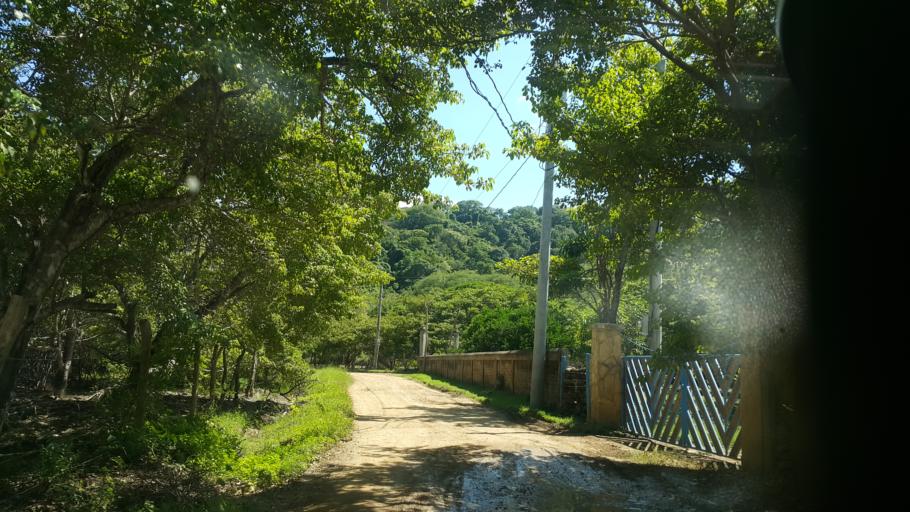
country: NI
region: Rivas
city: San Juan del Sur
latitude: 11.2850
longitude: -85.9014
